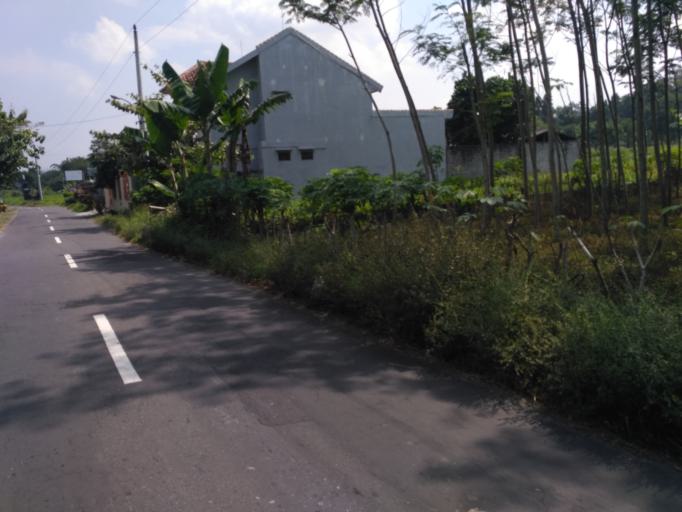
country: ID
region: Daerah Istimewa Yogyakarta
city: Depok
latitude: -7.7189
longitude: 110.4192
